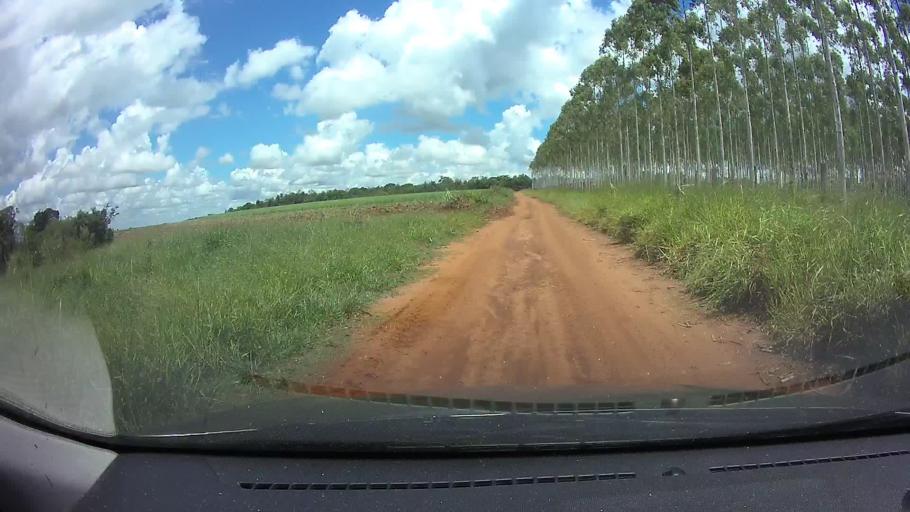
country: PY
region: Paraguari
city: La Colmena
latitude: -25.9652
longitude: -56.7330
